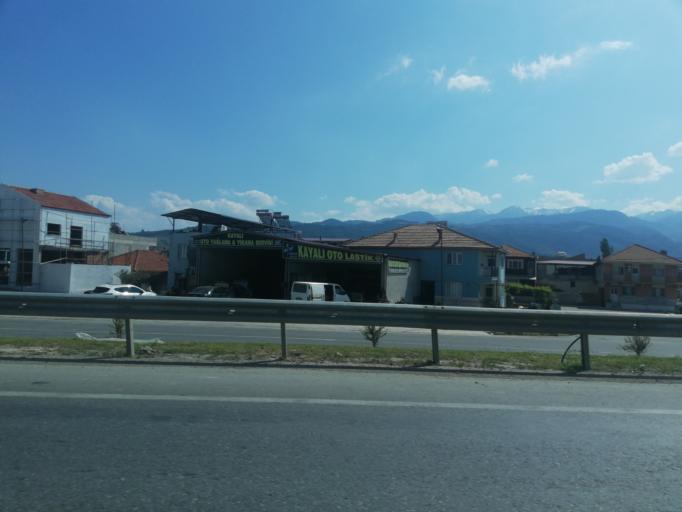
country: TR
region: Manisa
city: Alasehir
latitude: 38.3588
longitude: 28.5408
